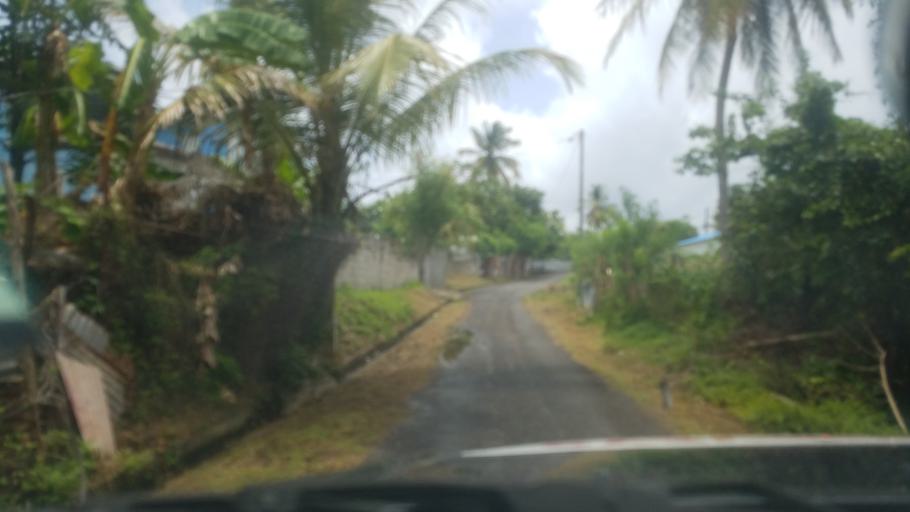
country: LC
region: Laborie Quarter
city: Laborie
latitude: 13.7438
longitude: -60.9571
